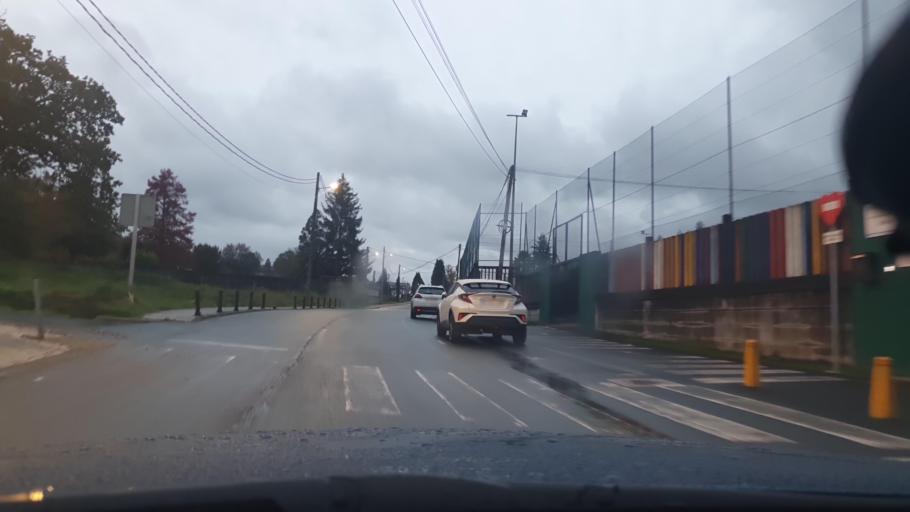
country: ES
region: Galicia
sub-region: Provincia da Coruna
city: Santiago de Compostela
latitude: 42.8512
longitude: -8.5888
